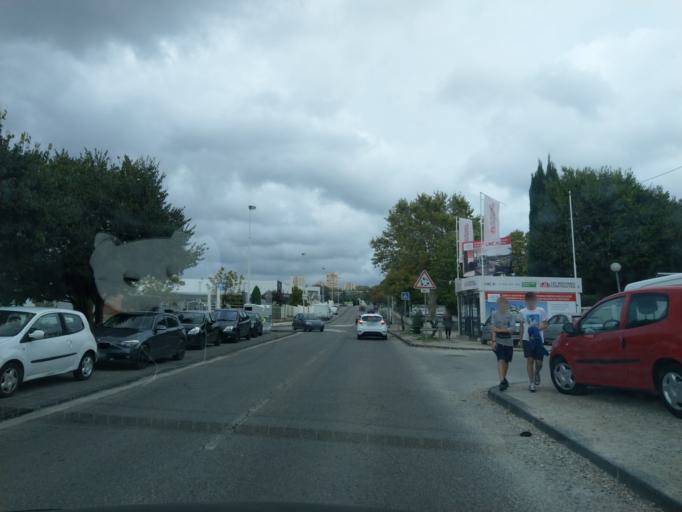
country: FR
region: Provence-Alpes-Cote d'Azur
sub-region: Departement des Bouches-du-Rhone
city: Marseille 12
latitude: 43.2956
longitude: 5.4274
